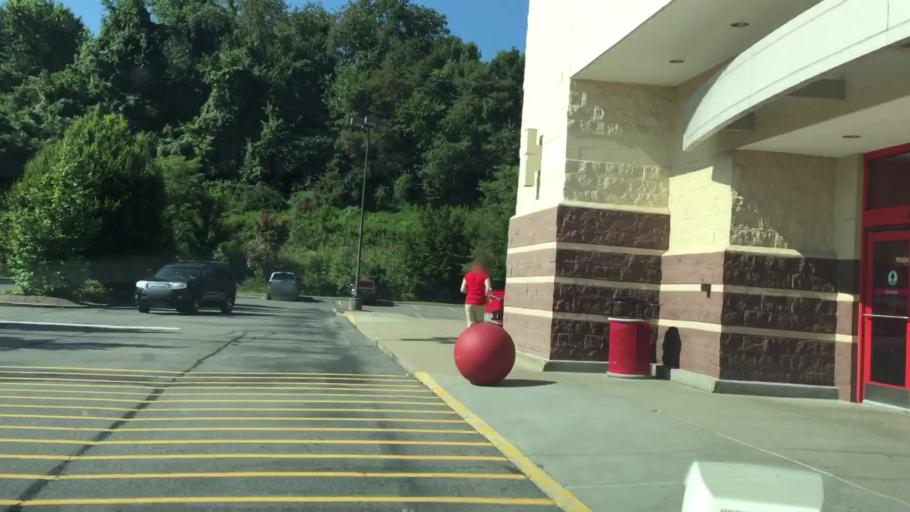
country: US
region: Pennsylvania
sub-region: Allegheny County
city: Oakdale
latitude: 40.4462
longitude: -80.1825
